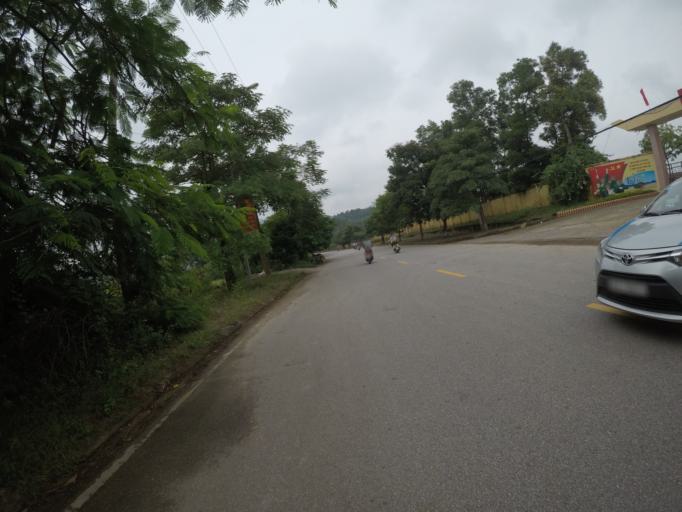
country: VN
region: Ha Noi
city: Soc Son
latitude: 21.2828
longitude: 105.8416
